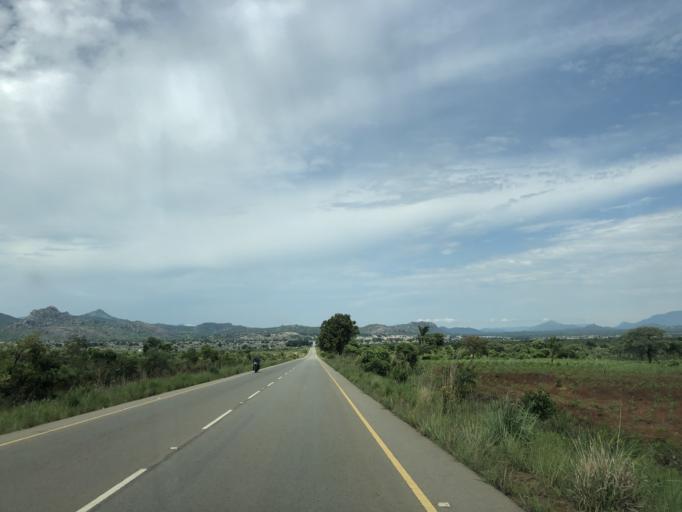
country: AO
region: Cuanza Sul
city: Quibala
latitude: -10.7339
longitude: 15.0113
